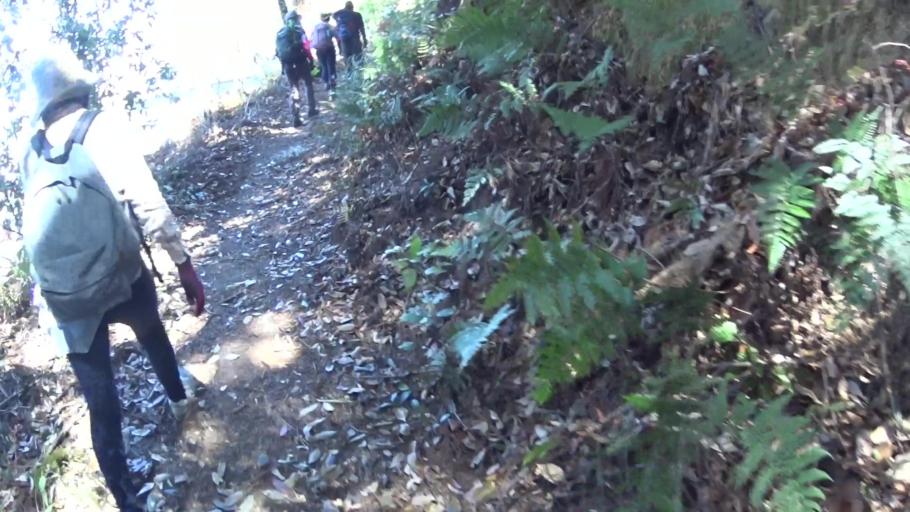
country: JP
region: Kyoto
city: Kyoto
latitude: 34.9851
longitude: 135.7827
